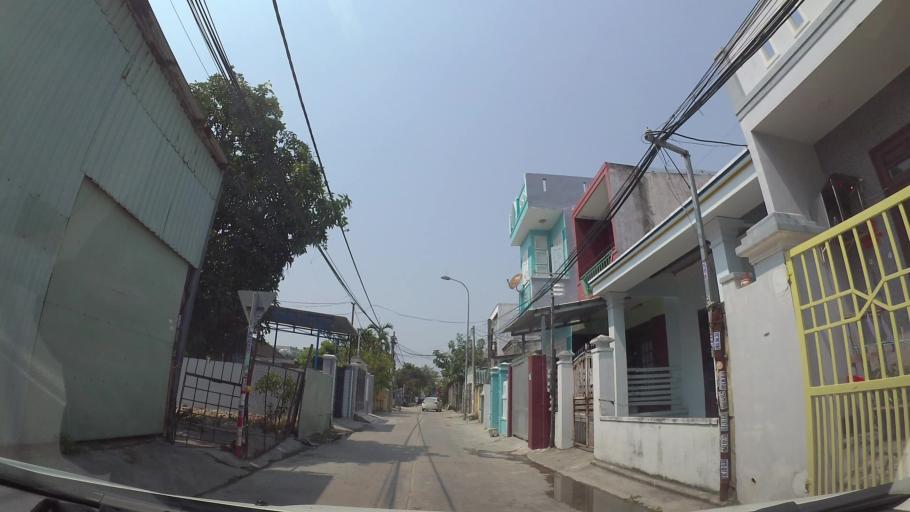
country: VN
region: Da Nang
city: Ngu Hanh Son
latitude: 16.0079
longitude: 108.2578
